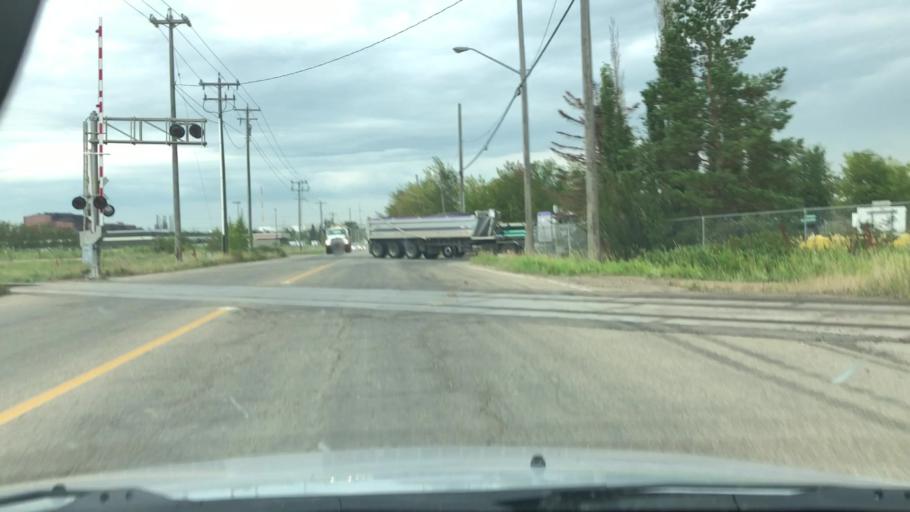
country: CA
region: Alberta
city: Edmonton
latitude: 53.5267
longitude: -113.4012
